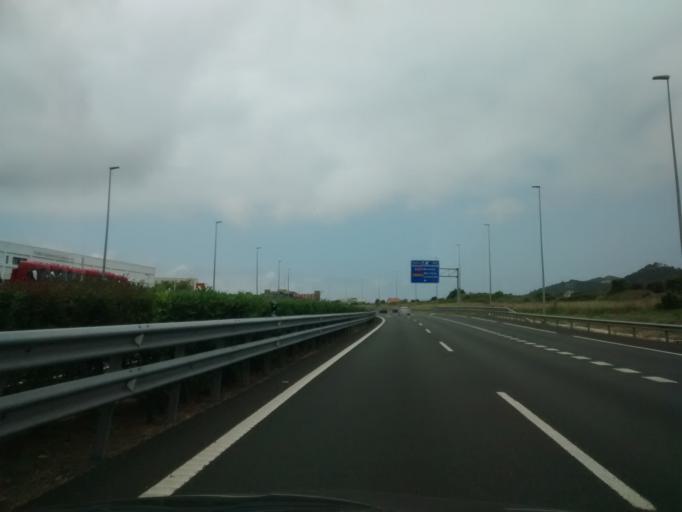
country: ES
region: Cantabria
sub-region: Provincia de Cantabria
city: Santa Cruz de Bezana
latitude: 43.4372
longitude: -3.9079
